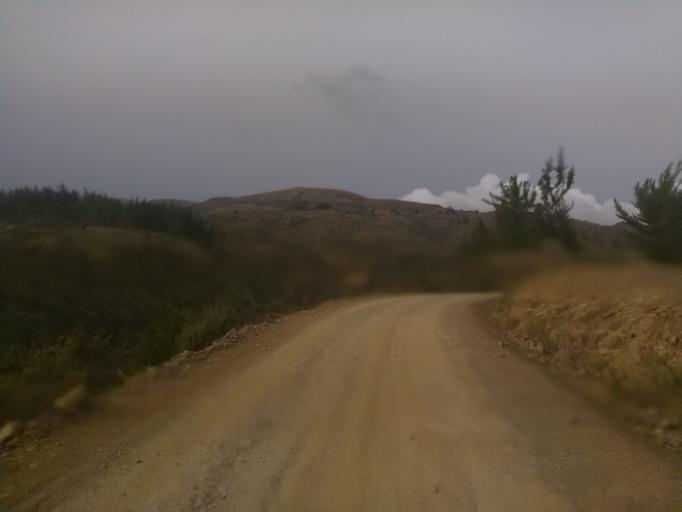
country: BO
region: Cochabamba
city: Cochabamba
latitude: -17.3016
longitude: -66.2188
